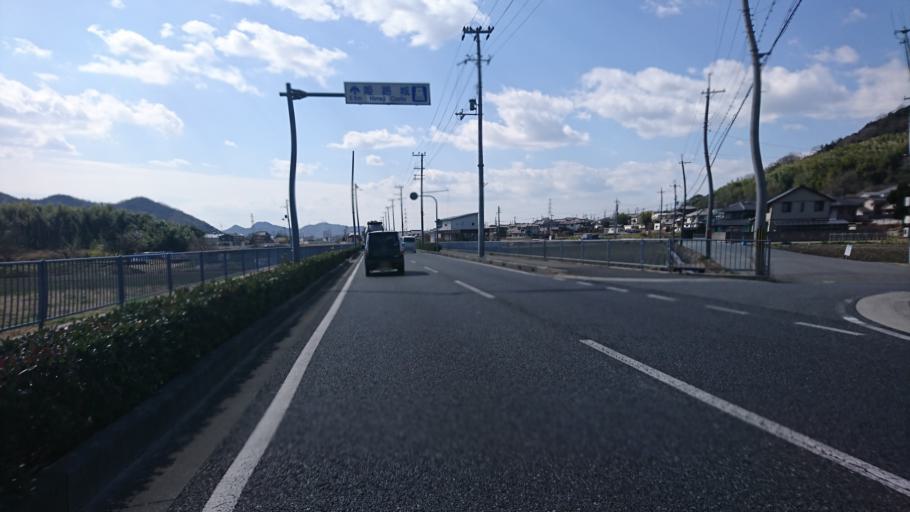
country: JP
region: Hyogo
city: Himeji
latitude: 34.8451
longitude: 134.7487
